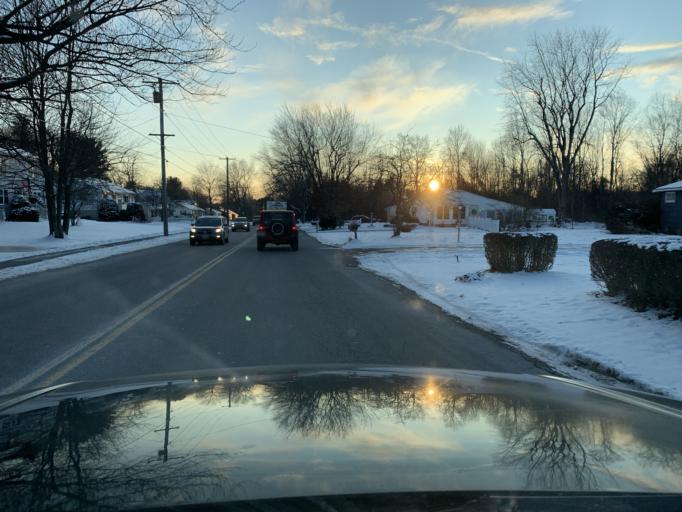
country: US
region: Massachusetts
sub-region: Essex County
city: Haverhill
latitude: 42.7855
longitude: -71.1105
